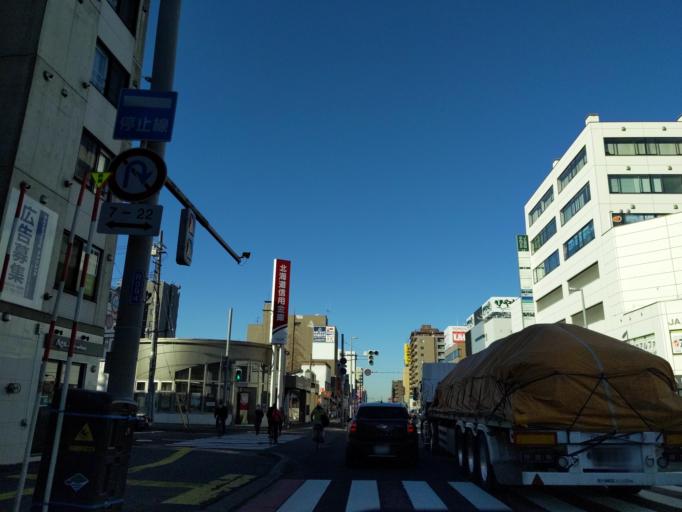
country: JP
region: Hokkaido
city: Sapporo
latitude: 43.0297
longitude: 141.3968
